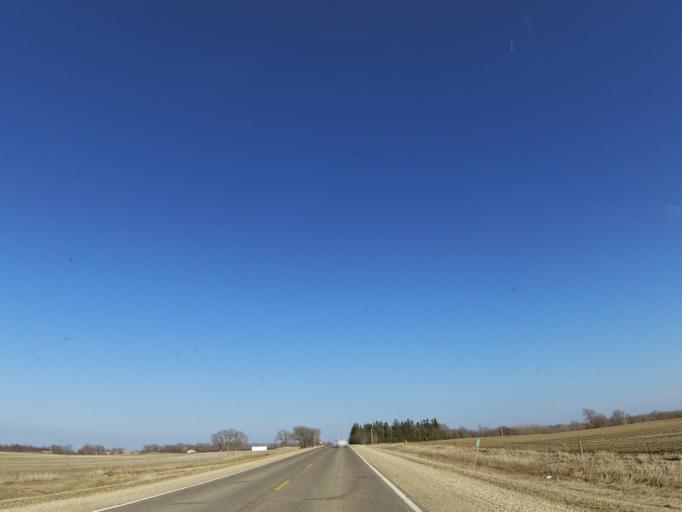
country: US
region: Iowa
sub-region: Worth County
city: Northwood
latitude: 43.4443
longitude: -93.2790
